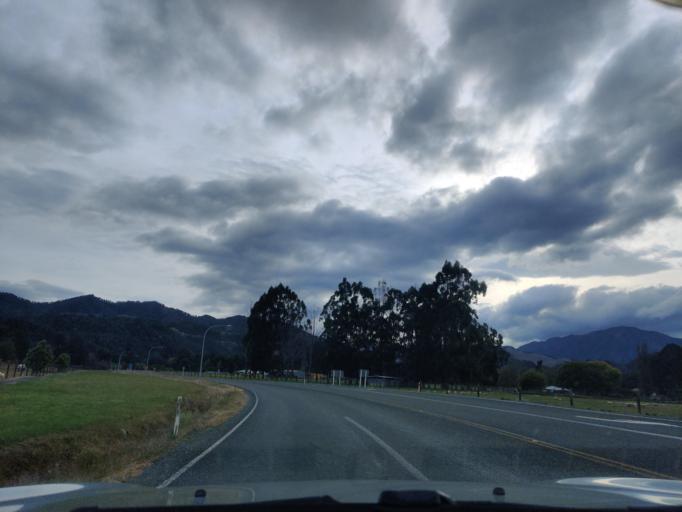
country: NZ
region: West Coast
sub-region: Buller District
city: Westport
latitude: -41.7997
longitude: 172.3363
